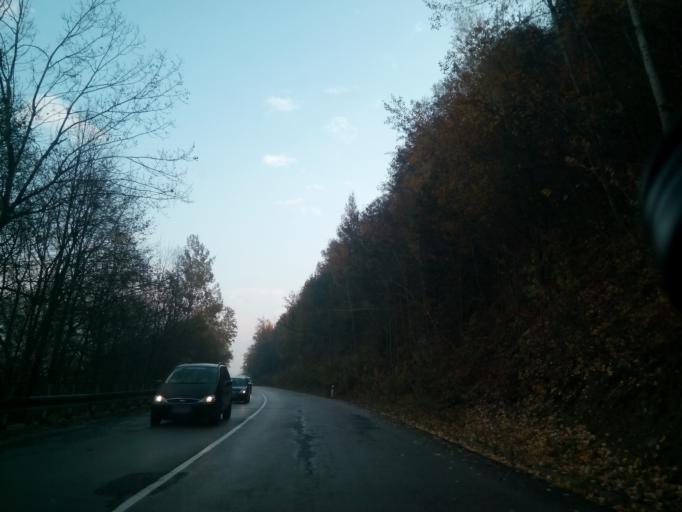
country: SK
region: Kosicky
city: Gelnica
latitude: 48.8965
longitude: 20.9914
